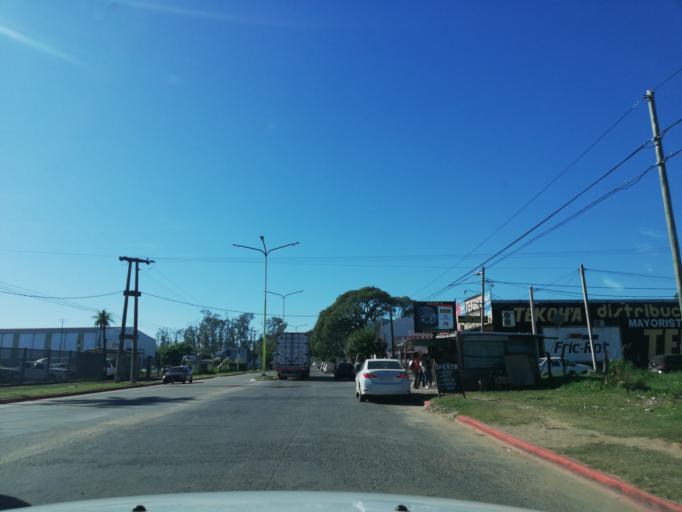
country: AR
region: Corrientes
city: Corrientes
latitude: -27.4761
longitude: -58.7928
